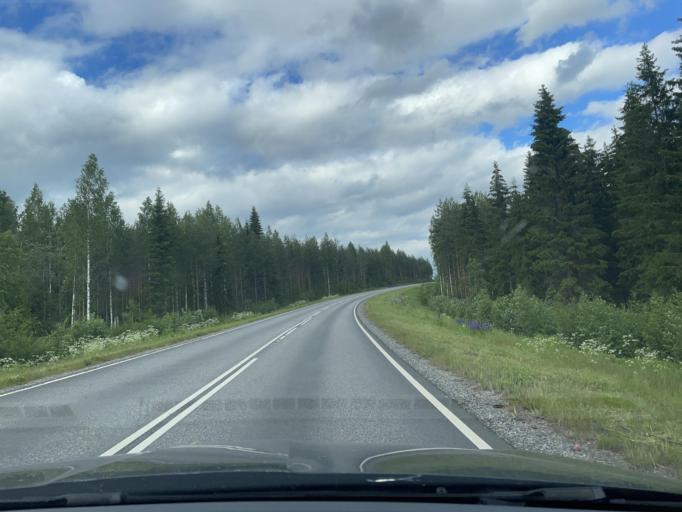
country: FI
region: Central Finland
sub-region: Jyvaeskylae
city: Petaejaevesi
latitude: 62.2173
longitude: 25.1505
